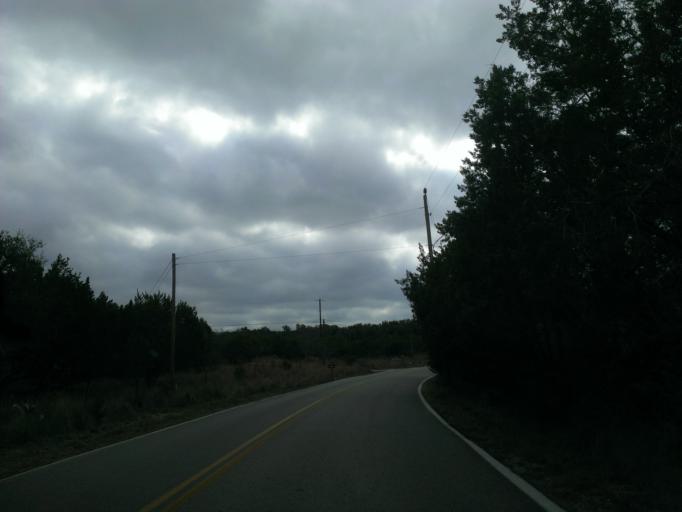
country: US
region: Texas
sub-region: Travis County
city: Briarcliff
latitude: 30.3729
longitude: -98.0859
